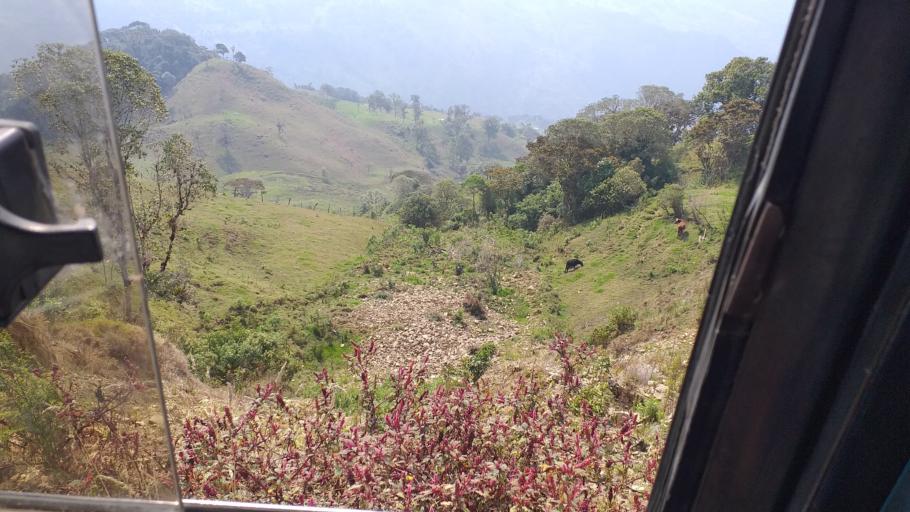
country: CO
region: Boyaca
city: Aquitania
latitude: 5.3623
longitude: -72.9228
